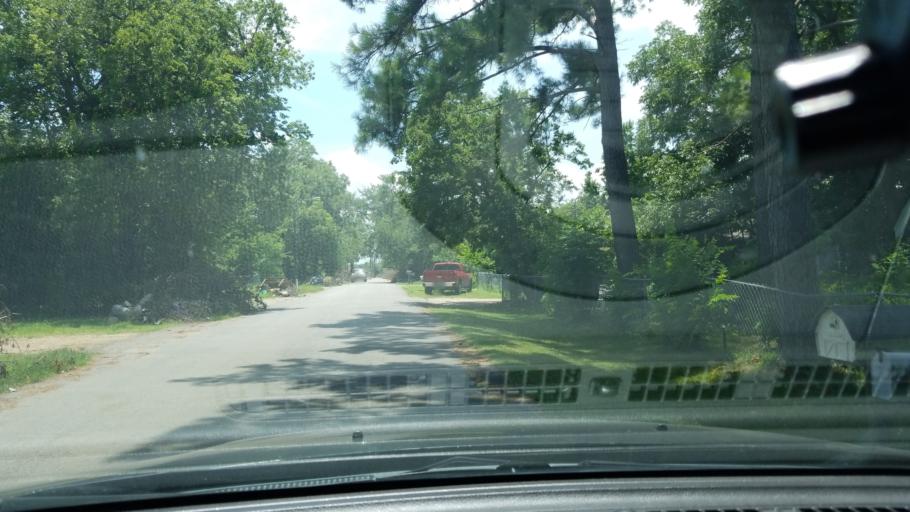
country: US
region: Texas
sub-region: Dallas County
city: Balch Springs
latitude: 32.7504
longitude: -96.6505
